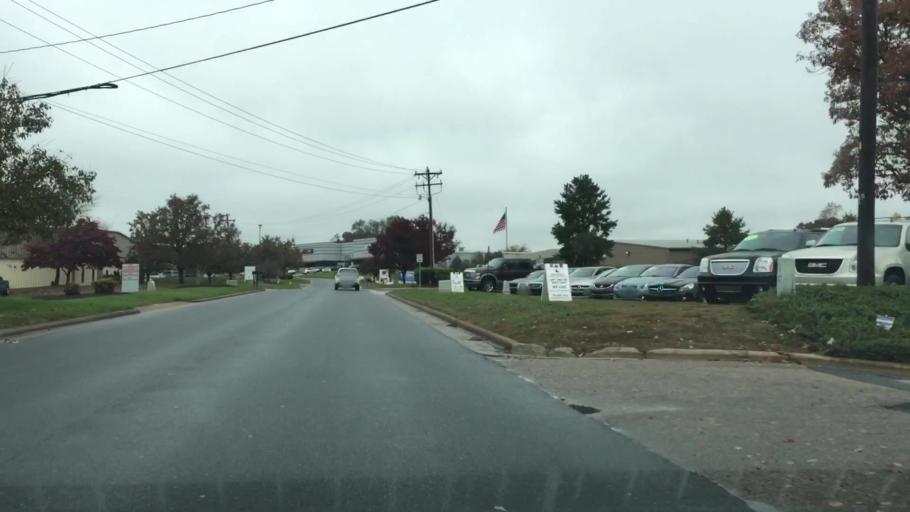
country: US
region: North Carolina
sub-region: Iredell County
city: Mooresville
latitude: 35.5858
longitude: -80.8608
